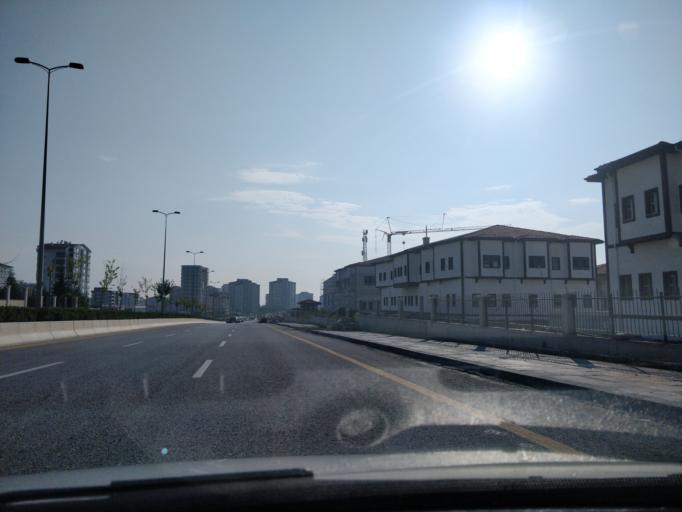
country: TR
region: Ankara
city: Etimesgut
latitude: 39.8951
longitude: 32.6331
